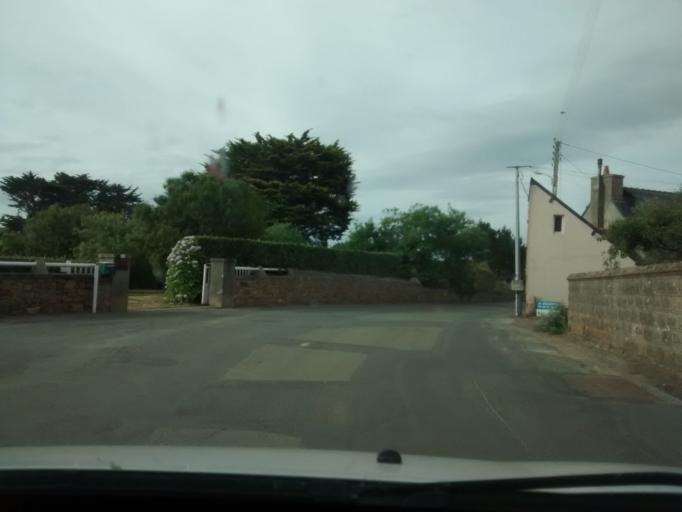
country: FR
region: Brittany
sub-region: Departement des Cotes-d'Armor
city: Penvenan
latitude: 48.8388
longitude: -3.2800
